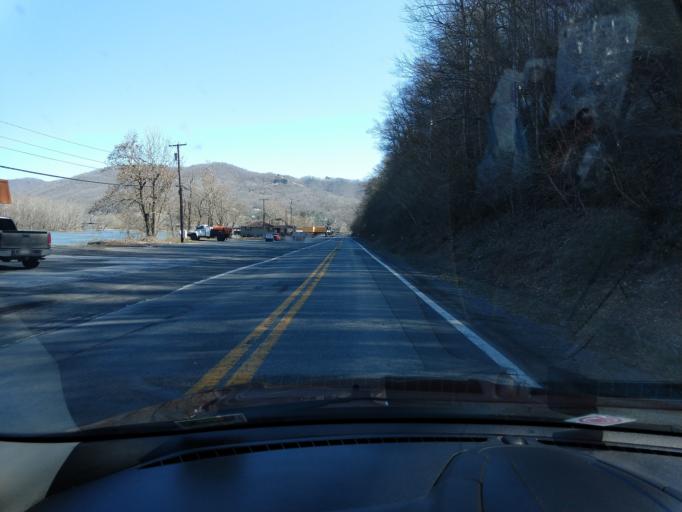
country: US
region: West Virginia
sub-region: Summers County
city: Hinton
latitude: 37.6549
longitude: -80.8932
